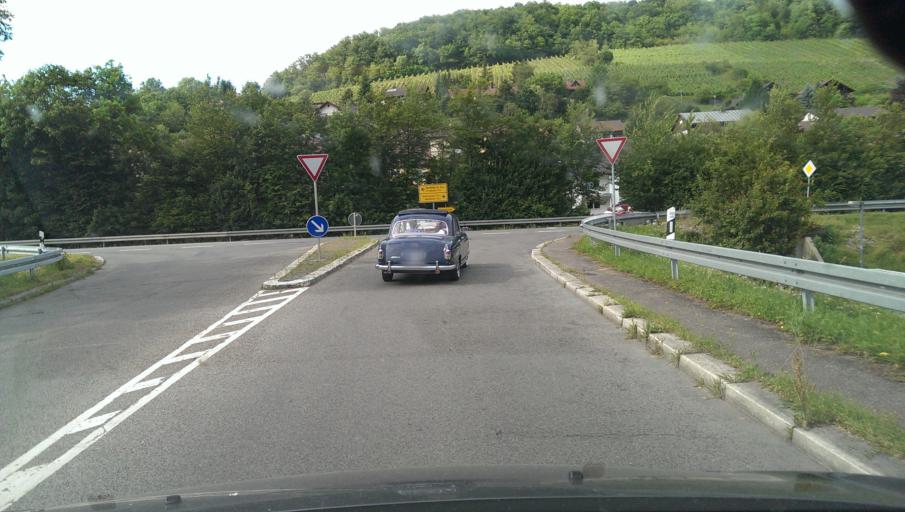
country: DE
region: Baden-Wuerttemberg
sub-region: Regierungsbezirk Stuttgart
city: Forchtenberg
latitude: 49.2920
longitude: 9.5611
